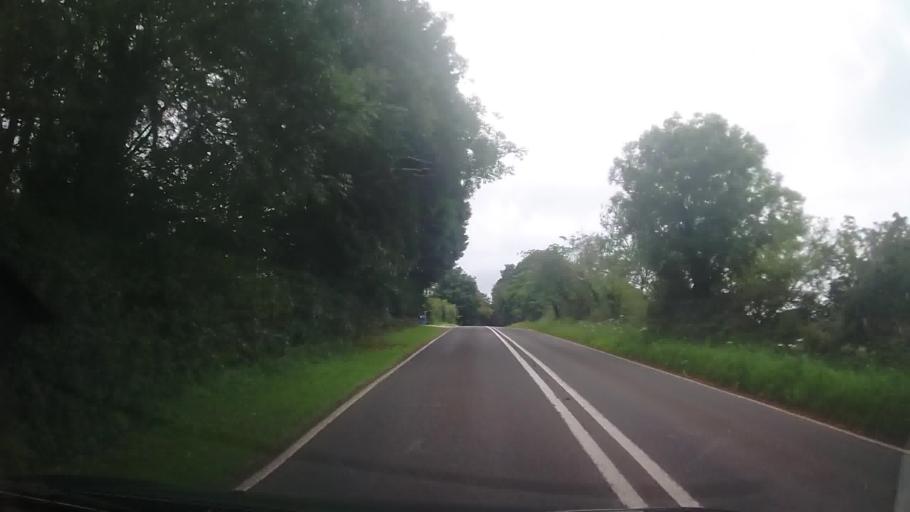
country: GB
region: Wales
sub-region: Anglesey
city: Gaerwen
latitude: 53.1894
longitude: -4.2514
